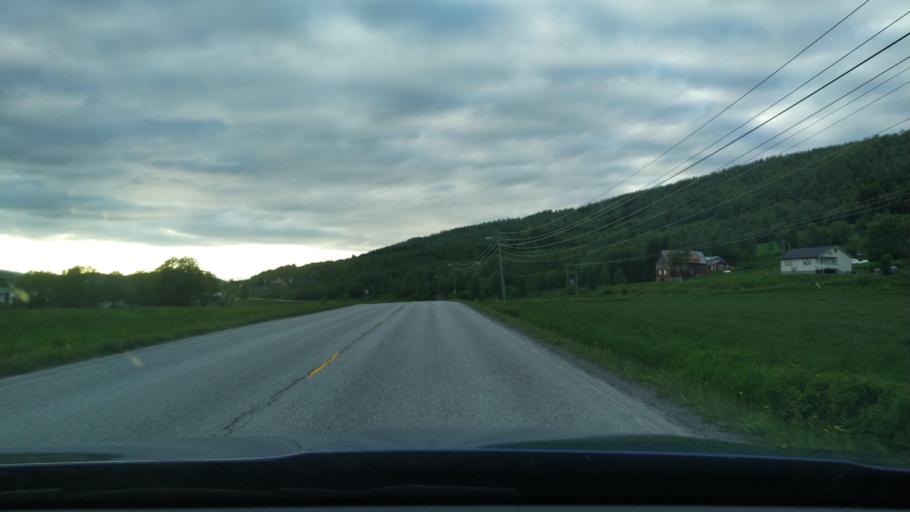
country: NO
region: Troms
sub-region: Sorreisa
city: Sorreisa
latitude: 69.1251
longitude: 18.2155
